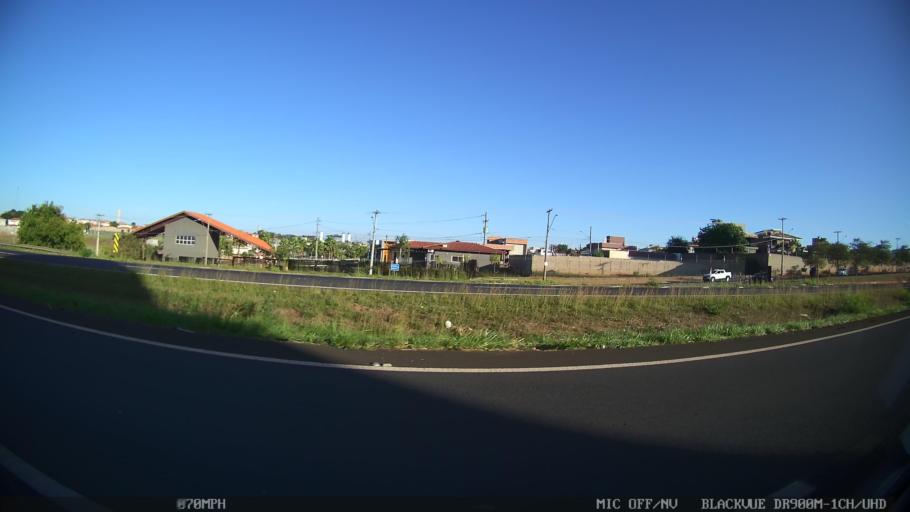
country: BR
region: Sao Paulo
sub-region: Sao Jose Do Rio Preto
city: Sao Jose do Rio Preto
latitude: -20.8001
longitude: -49.3364
